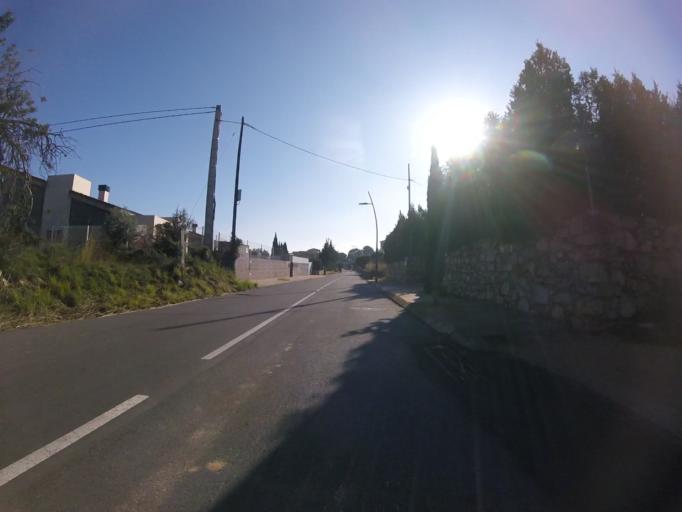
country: ES
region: Valencia
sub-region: Provincia de Castello
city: Peniscola
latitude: 40.3843
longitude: 0.3803
